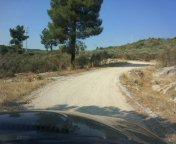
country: PT
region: Viseu
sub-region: Sernancelhe
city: Sernancelhe
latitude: 40.9350
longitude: -7.5083
